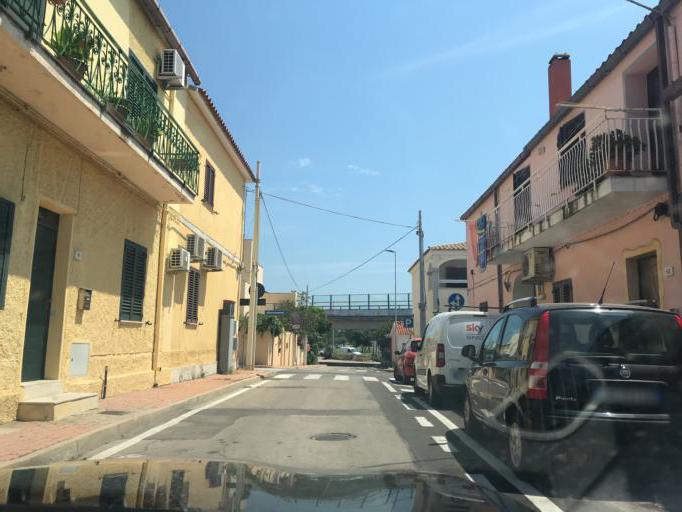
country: IT
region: Sardinia
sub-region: Provincia di Olbia-Tempio
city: Olbia
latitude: 40.9308
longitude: 9.5074
